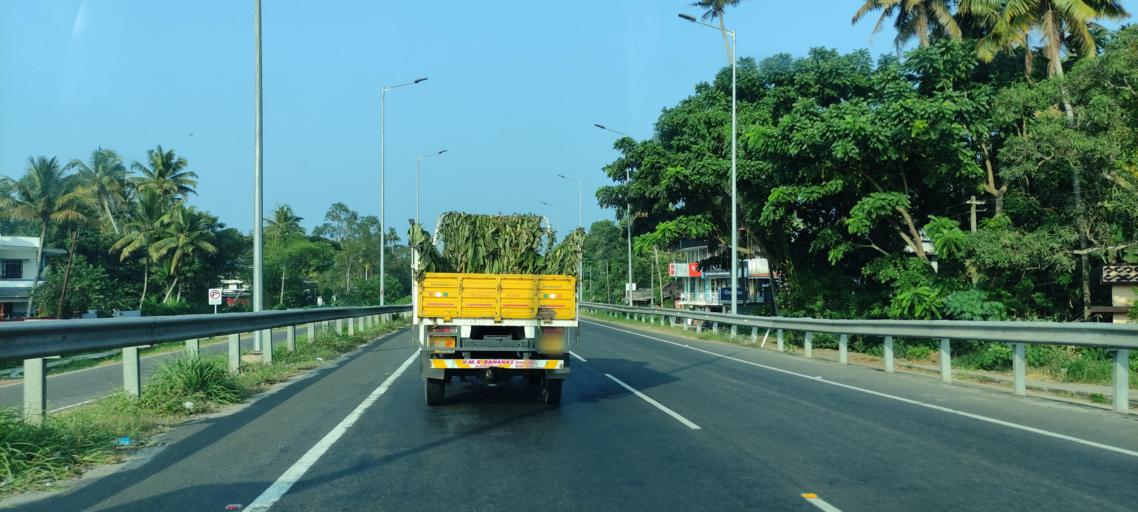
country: IN
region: Kerala
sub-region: Alappuzha
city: Alleppey
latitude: 9.5066
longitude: 76.3230
